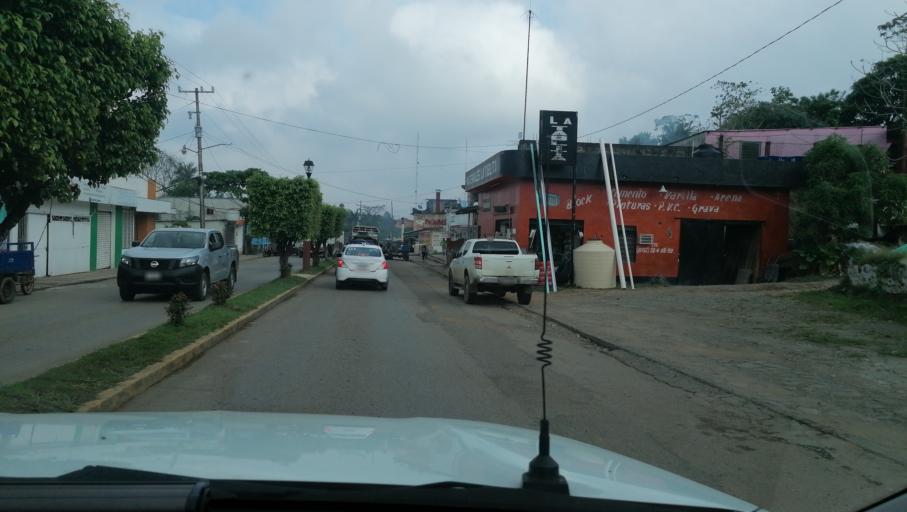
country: MX
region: Chiapas
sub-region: Juarez
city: El Triunfo 1ra. Seccion (Cardona)
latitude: 17.6065
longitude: -93.1914
